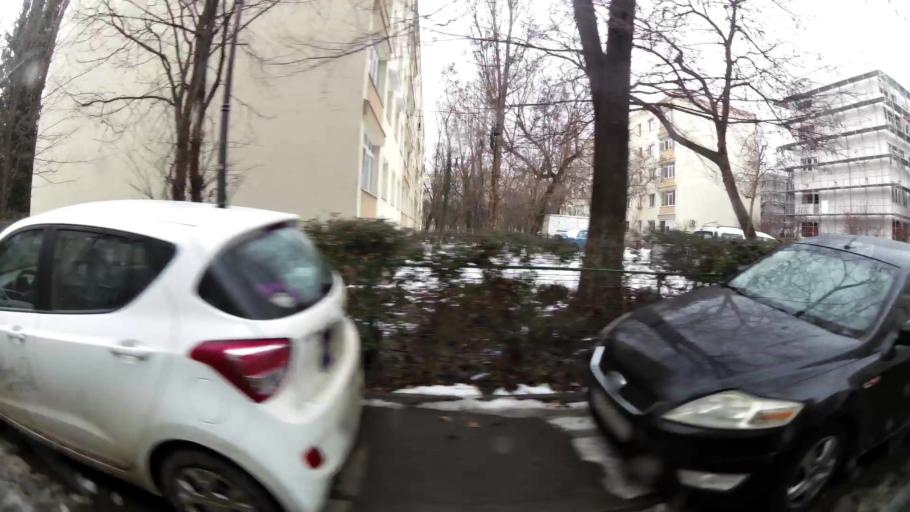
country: RO
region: Ilfov
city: Dobroesti
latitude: 44.4159
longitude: 26.1813
